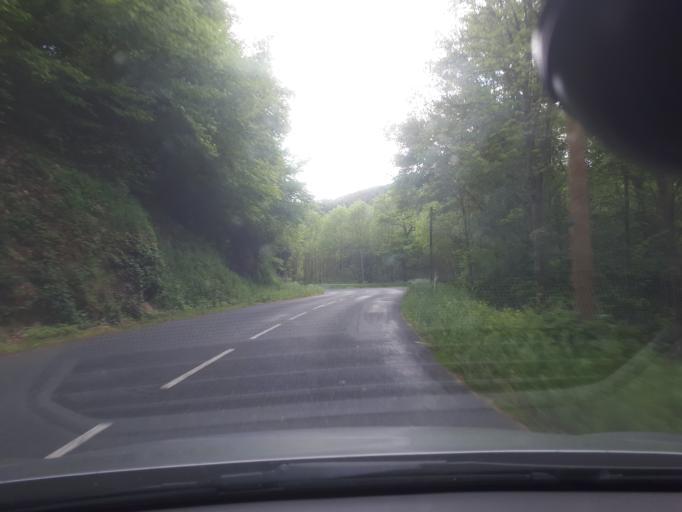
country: FR
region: Rhone-Alpes
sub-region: Departement du Rhone
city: Sainte-Foy-l'Argentiere
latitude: 45.7091
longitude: 4.4424
